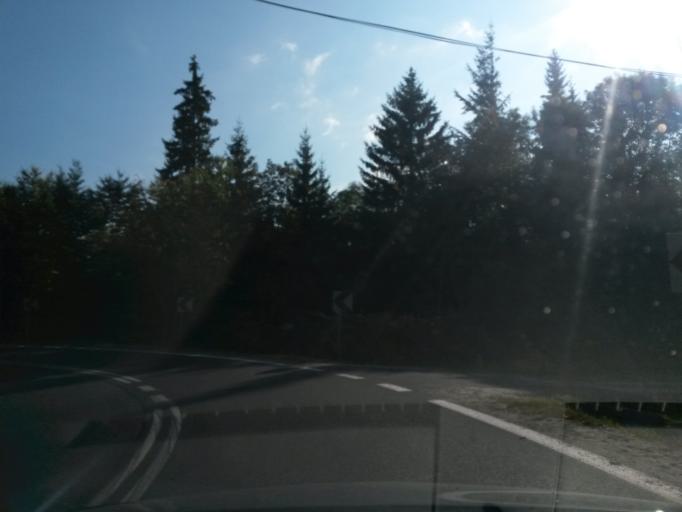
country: PL
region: Lower Silesian Voivodeship
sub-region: Powiat jeleniogorski
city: Szklarska Poreba
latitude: 50.8246
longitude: 15.5039
